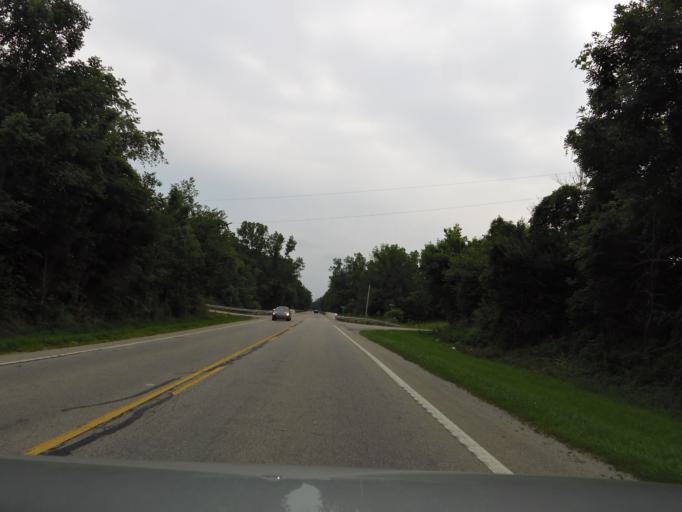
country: US
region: Ohio
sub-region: Brown County
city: Mount Orab
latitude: 38.9670
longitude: -83.9146
